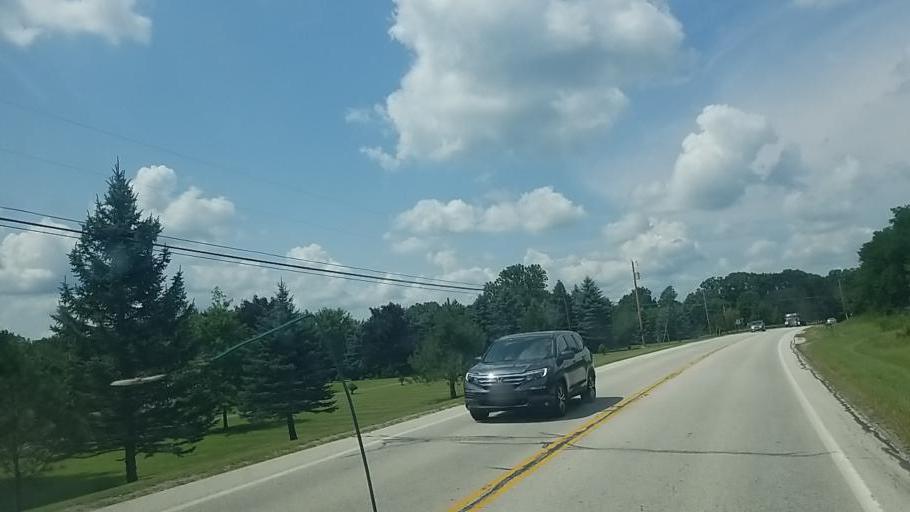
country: US
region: Ohio
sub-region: Medina County
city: Lodi
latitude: 41.0262
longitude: -82.0756
